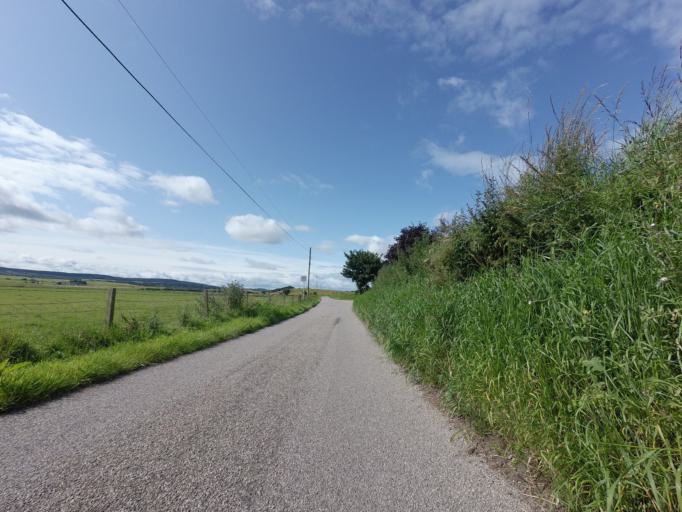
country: GB
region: Scotland
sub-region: Moray
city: Burghead
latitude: 57.6498
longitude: -3.5043
